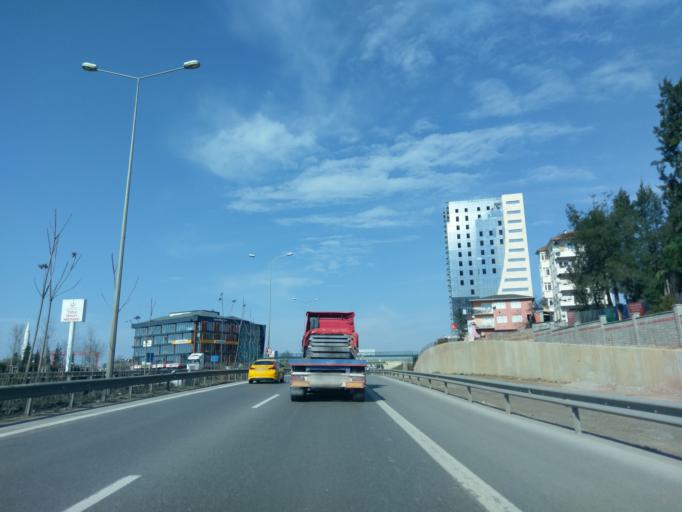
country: TR
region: Istanbul
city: Icmeler
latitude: 40.8456
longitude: 29.3033
